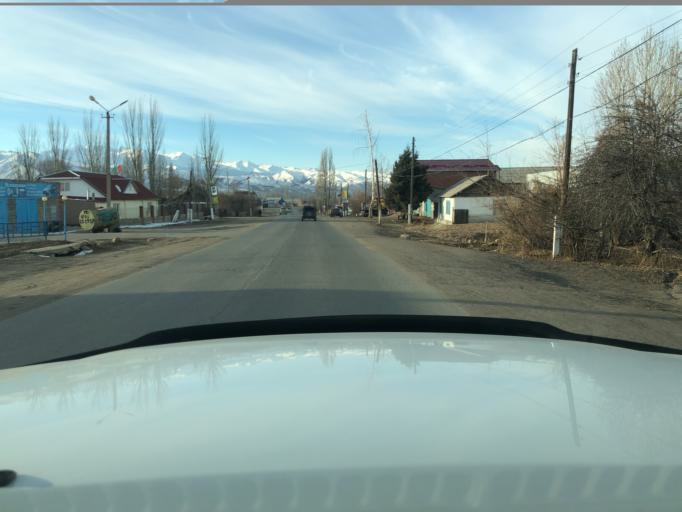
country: KG
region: Ysyk-Koel
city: Pokrovka
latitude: 42.3481
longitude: 78.0154
